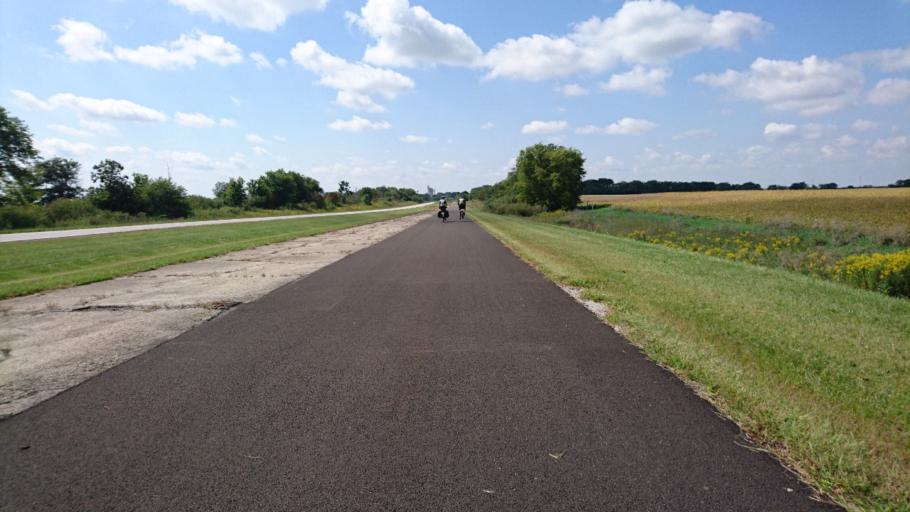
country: US
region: Illinois
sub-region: McLean County
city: Hudson
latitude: 40.5763
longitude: -88.8802
